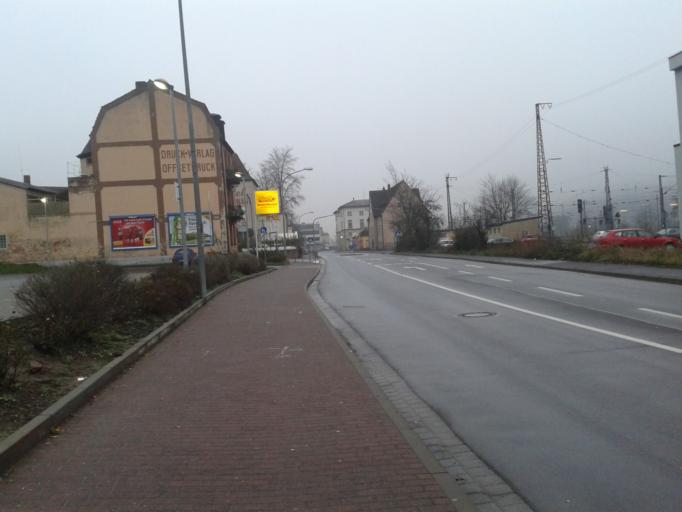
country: DE
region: Bavaria
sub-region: Regierungsbezirk Unterfranken
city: Gemunden
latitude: 50.0520
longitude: 9.6980
